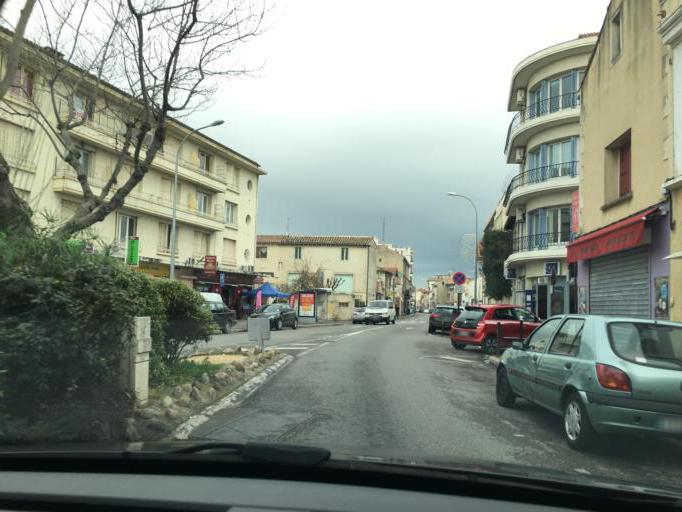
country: FR
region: Provence-Alpes-Cote d'Azur
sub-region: Departement du Vaucluse
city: Avignon
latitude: 43.9363
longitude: 4.8104
